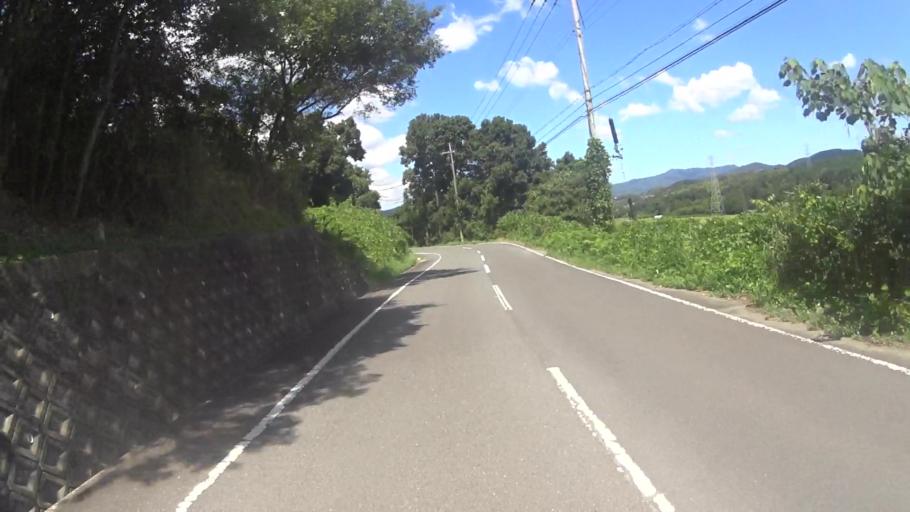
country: JP
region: Nara
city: Nara-shi
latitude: 34.7279
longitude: 135.8640
